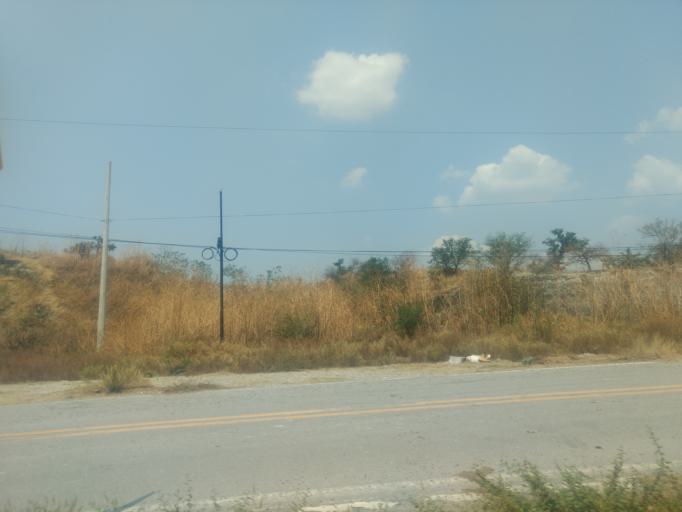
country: MX
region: Morelos
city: Ahuehuetzingo
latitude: 18.6694
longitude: -99.2973
